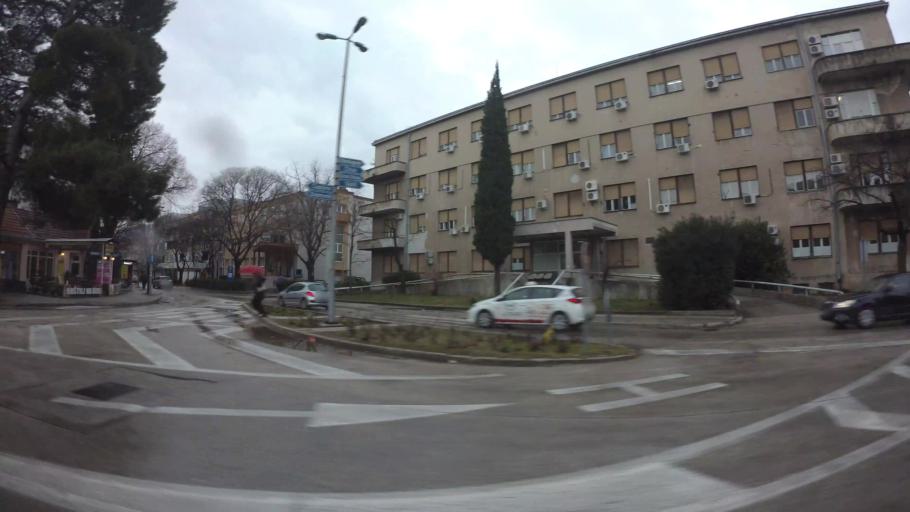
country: BA
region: Federation of Bosnia and Herzegovina
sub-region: Hercegovacko-Bosanski Kanton
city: Mostar
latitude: 43.3469
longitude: 17.8046
